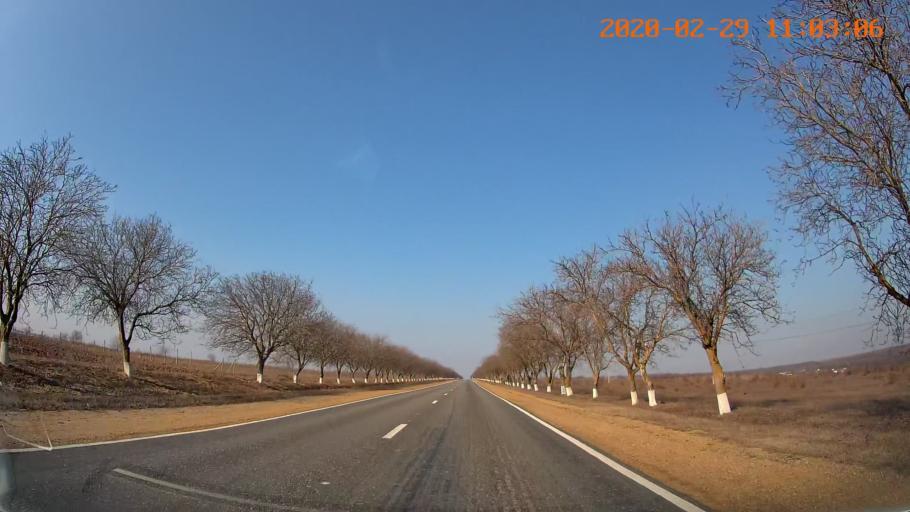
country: MD
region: Criuleni
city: Criuleni
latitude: 47.1771
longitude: 29.2247
